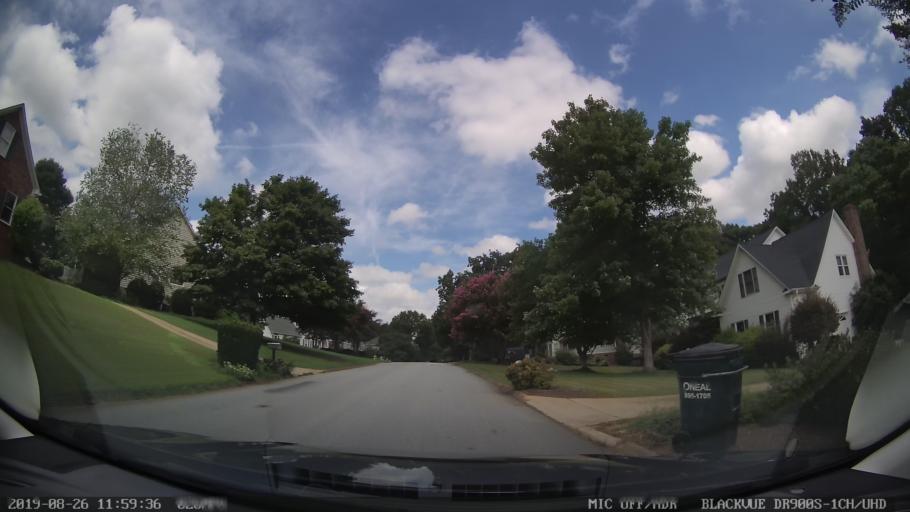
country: US
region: South Carolina
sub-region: Greenville County
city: Five Forks
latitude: 34.7968
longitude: -82.2342
